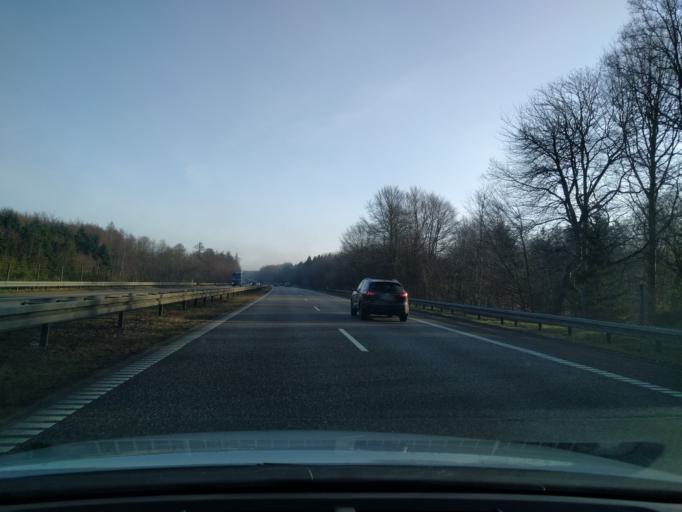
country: DK
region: Zealand
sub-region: Soro Kommune
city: Soro
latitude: 55.4365
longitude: 11.4895
